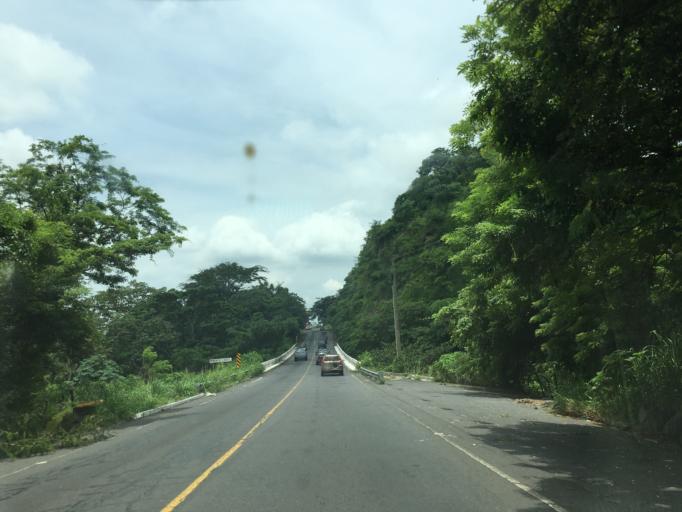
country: GT
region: Escuintla
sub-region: Municipio de Escuintla
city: Escuintla
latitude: 14.3569
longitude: -90.8082
